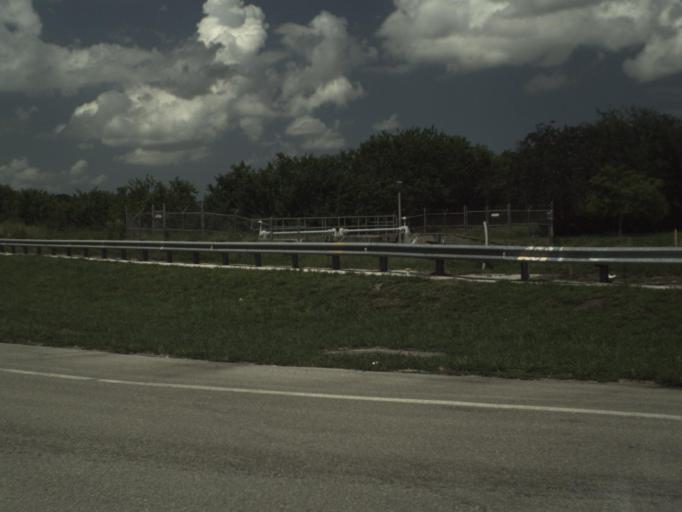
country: US
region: Florida
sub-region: Palm Beach County
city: Boca Pointe
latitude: 26.3710
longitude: -80.2034
